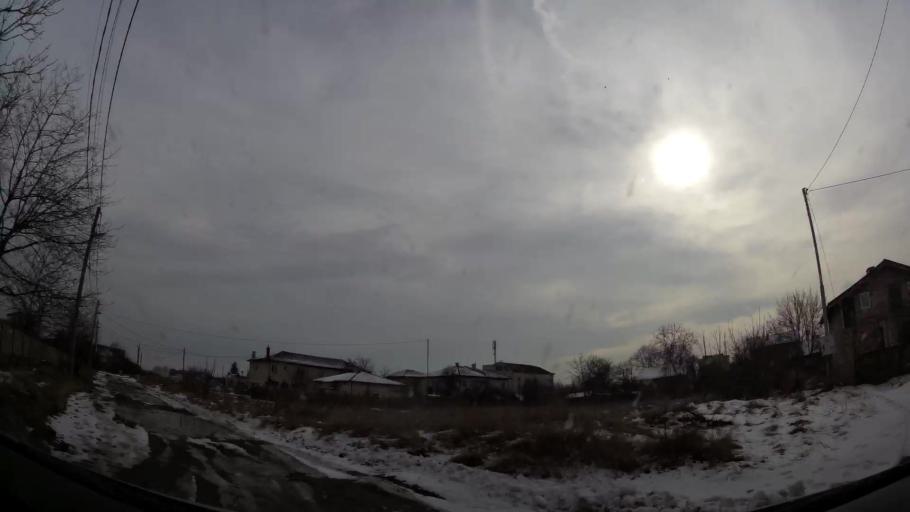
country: BG
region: Sofia-Capital
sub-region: Stolichna Obshtina
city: Sofia
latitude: 42.7100
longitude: 23.4133
